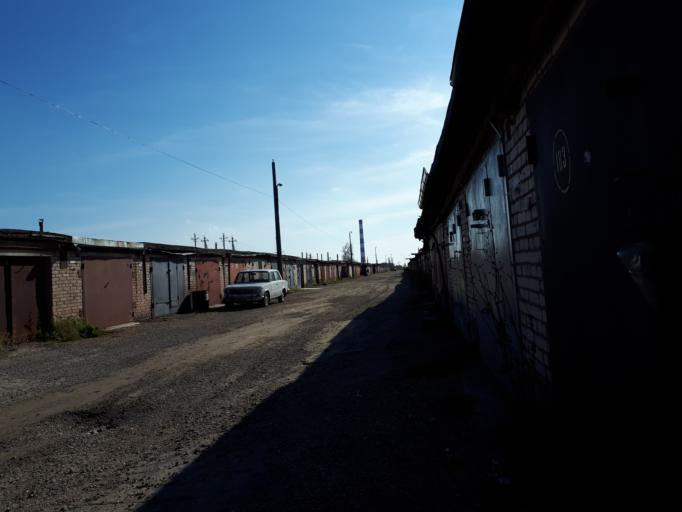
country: BY
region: Vitebsk
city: Vitebsk
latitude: 55.1665
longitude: 30.2450
